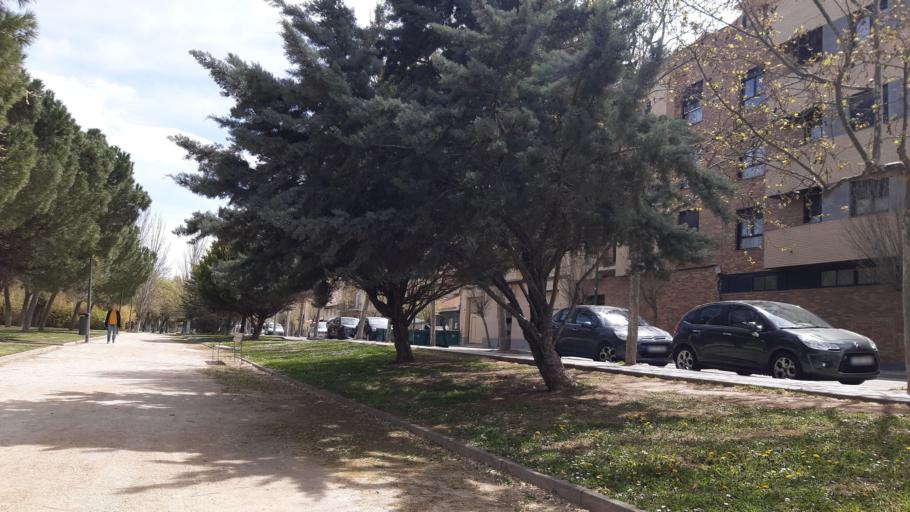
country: ES
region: Aragon
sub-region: Provincia de Zaragoza
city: Utebo
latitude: 41.7129
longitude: -1.0051
